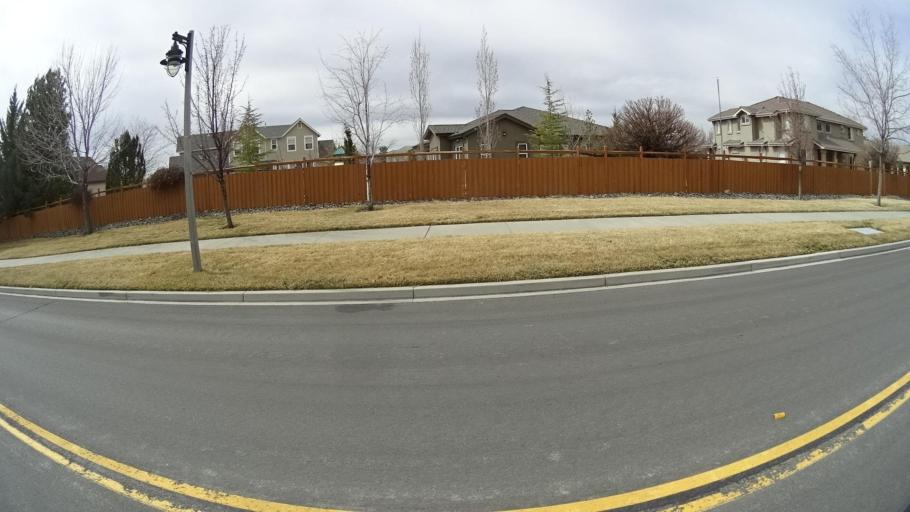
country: US
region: Nevada
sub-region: Washoe County
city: Spanish Springs
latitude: 39.6240
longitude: -119.6856
